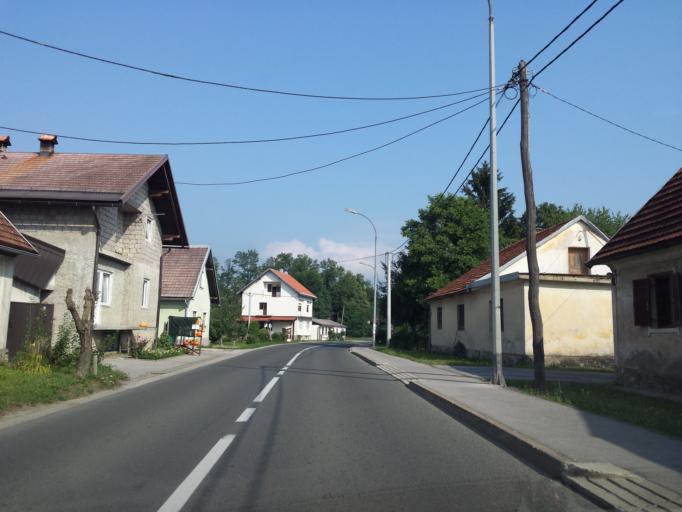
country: HR
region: Karlovacka
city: Ostarije
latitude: 45.2357
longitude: 15.2545
